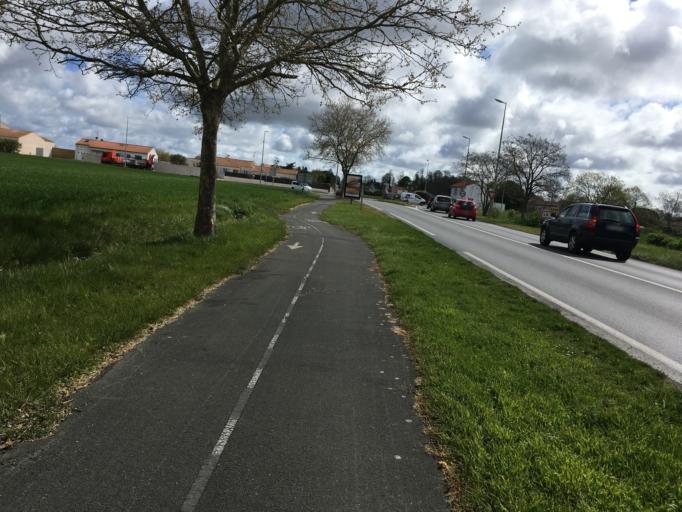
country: FR
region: Poitou-Charentes
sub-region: Departement de la Charente-Maritime
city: La Jarne
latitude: 46.1303
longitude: -1.0824
